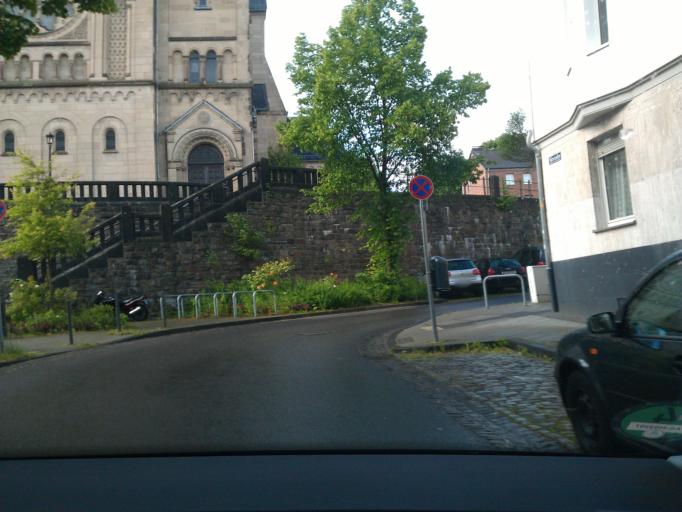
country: DE
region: North Rhine-Westphalia
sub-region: Regierungsbezirk Koln
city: Aachen
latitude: 50.7677
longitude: 6.1085
